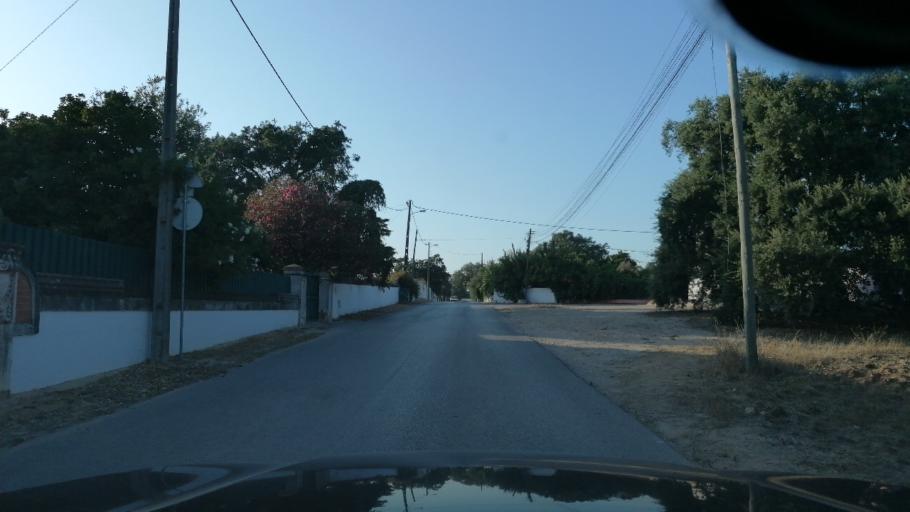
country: PT
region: Setubal
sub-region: Setubal
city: Setubal
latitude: 38.5450
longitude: -8.8398
